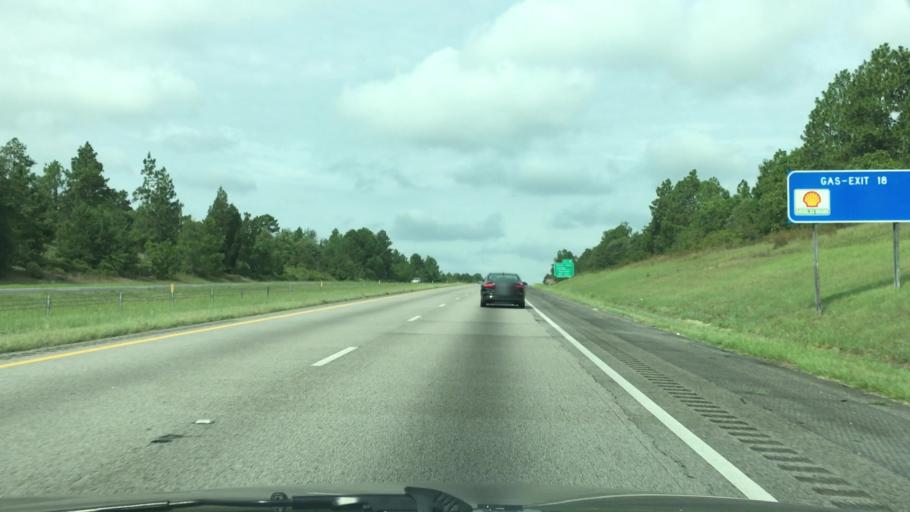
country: US
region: South Carolina
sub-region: Aiken County
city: Aiken
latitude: 33.6439
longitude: -81.7278
